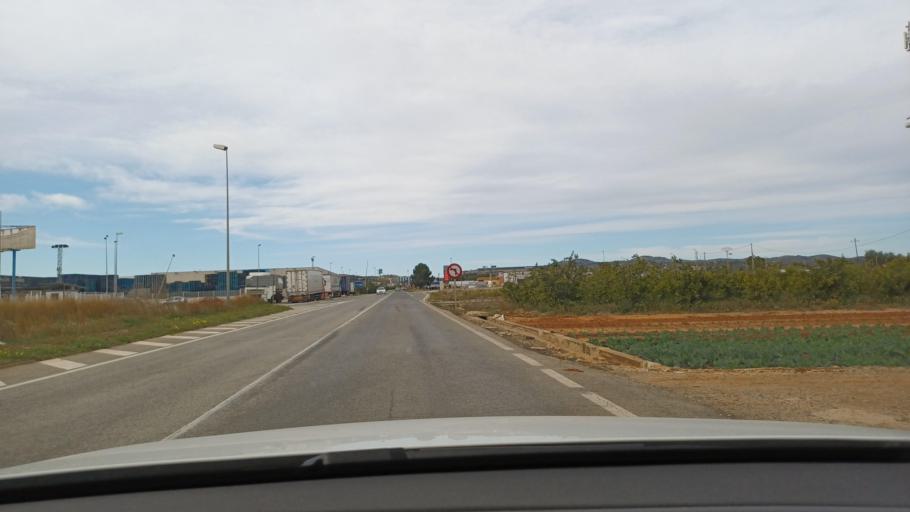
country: ES
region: Valencia
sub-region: Provincia de Valencia
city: Benifaio
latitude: 39.2883
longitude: -0.4471
